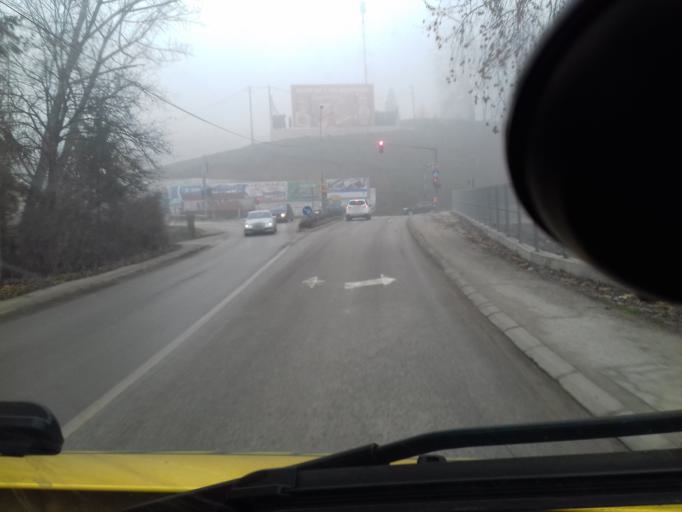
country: BA
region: Federation of Bosnia and Herzegovina
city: Vitez
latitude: 44.1504
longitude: 17.8062
